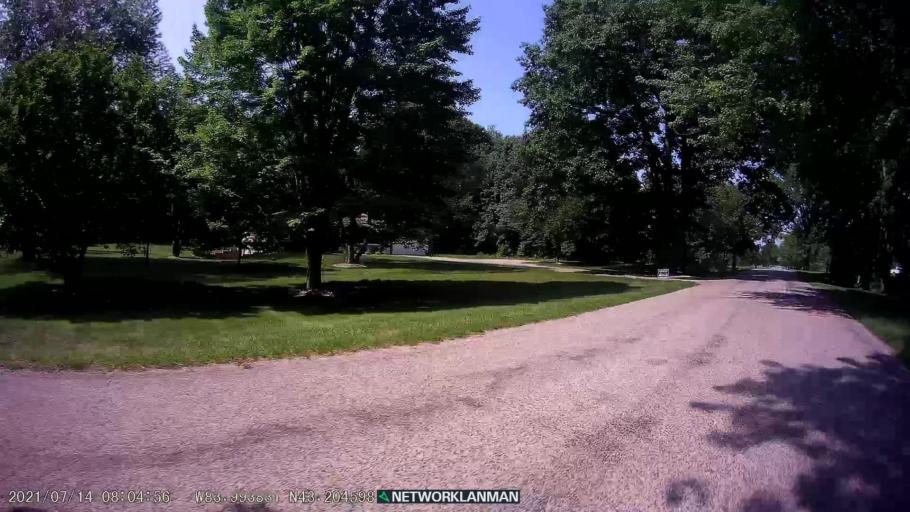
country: US
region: Michigan
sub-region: Saginaw County
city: Burt
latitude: 43.2046
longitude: -83.9942
